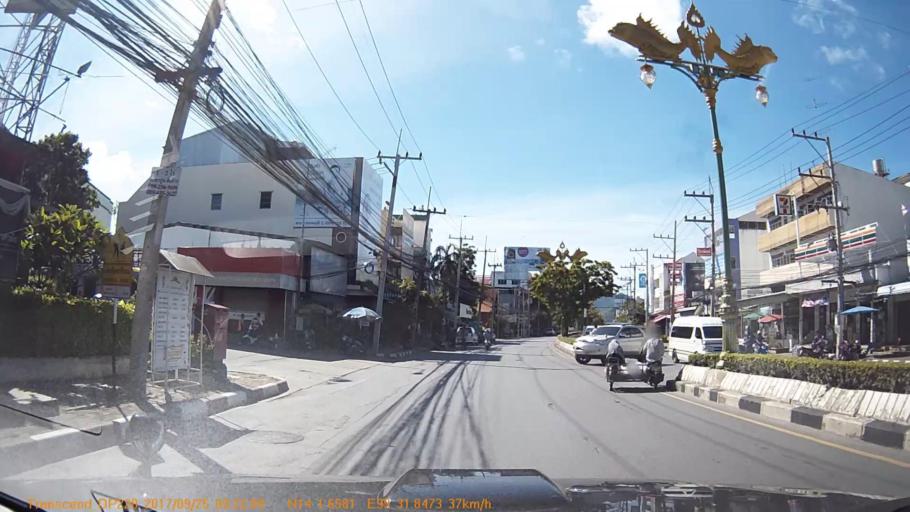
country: TH
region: Kanchanaburi
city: Kanchanaburi
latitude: 14.0276
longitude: 99.5308
